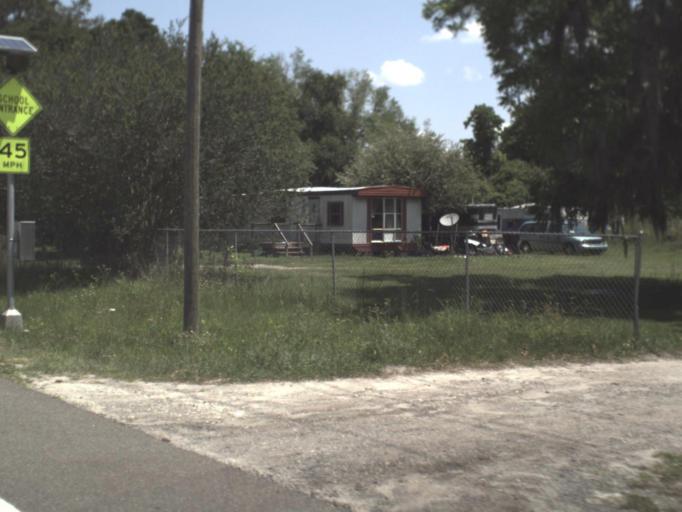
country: US
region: Florida
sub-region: Clay County
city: Keystone Heights
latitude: 29.8383
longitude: -82.0647
